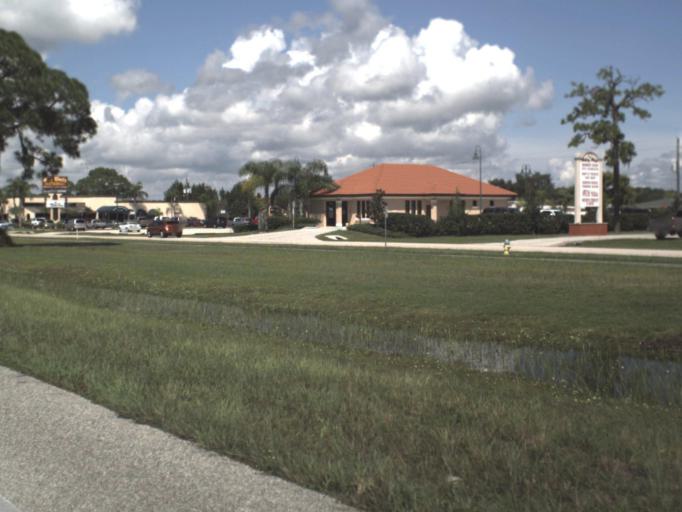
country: US
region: Florida
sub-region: Sarasota County
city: North Port
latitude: 27.0426
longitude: -82.2323
